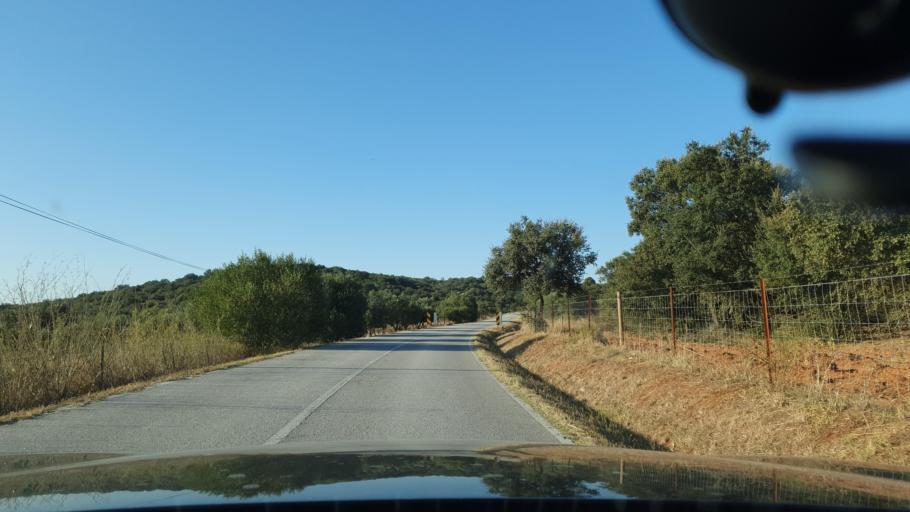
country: PT
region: Evora
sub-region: Estremoz
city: Estremoz
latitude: 38.9030
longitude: -7.6682
